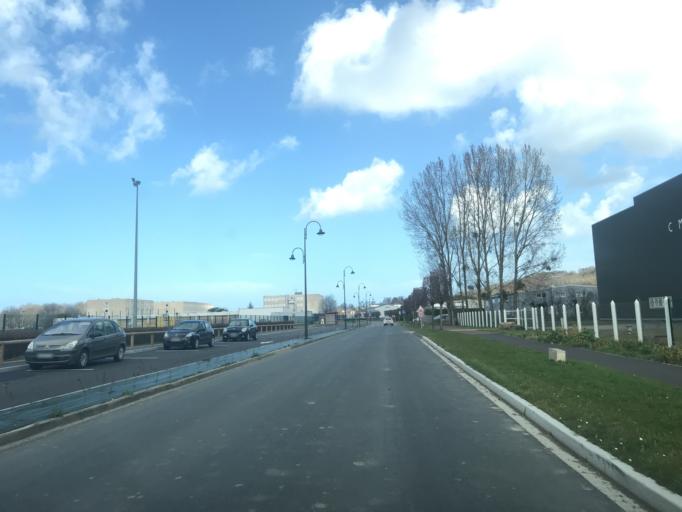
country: FR
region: Lower Normandy
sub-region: Departement du Calvados
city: Dives-sur-Mer
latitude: 49.2768
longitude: -0.0955
